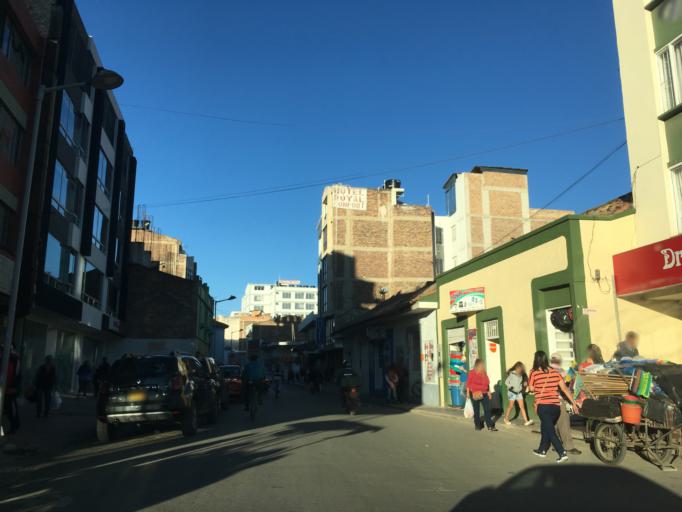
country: CO
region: Boyaca
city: Sogamoso
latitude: 5.7131
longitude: -72.9293
